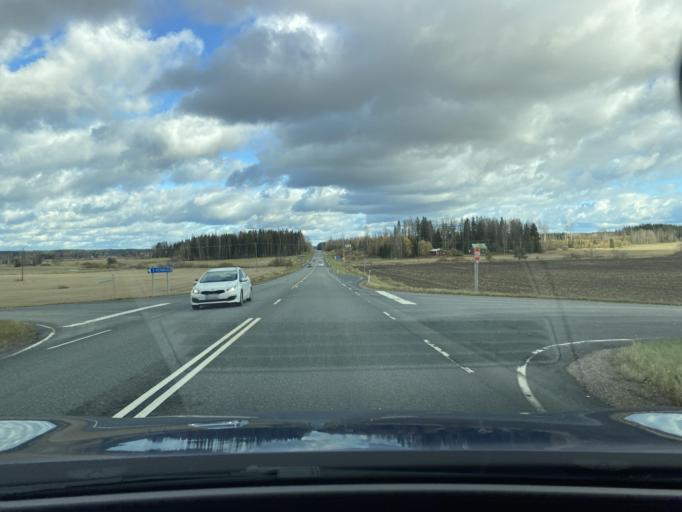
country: FI
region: Haeme
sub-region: Forssa
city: Humppila
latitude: 60.9410
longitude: 23.2844
